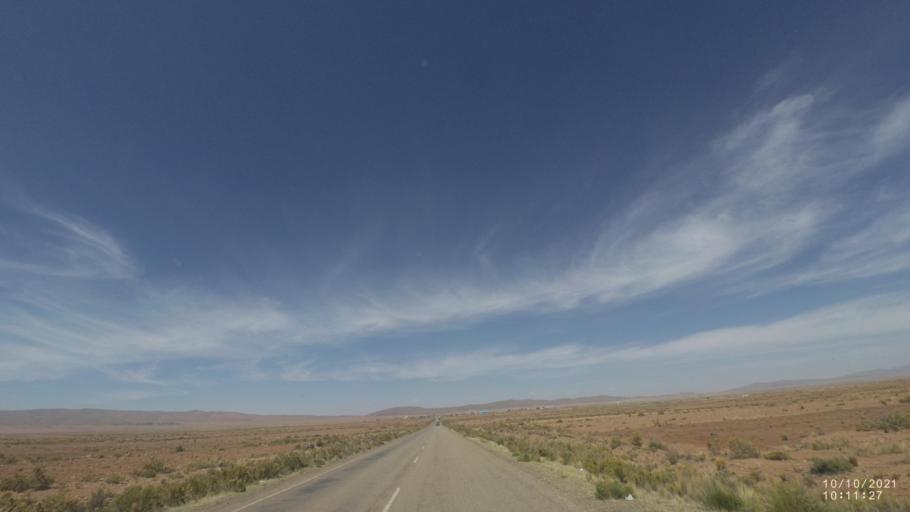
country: BO
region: La Paz
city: Eucaliptus
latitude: -17.4231
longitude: -67.5038
